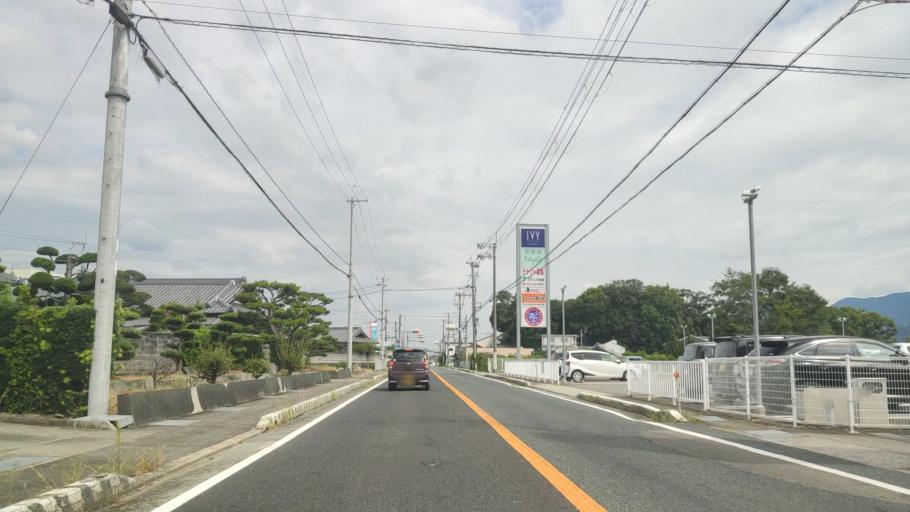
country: JP
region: Wakayama
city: Iwade
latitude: 34.2674
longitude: 135.3938
